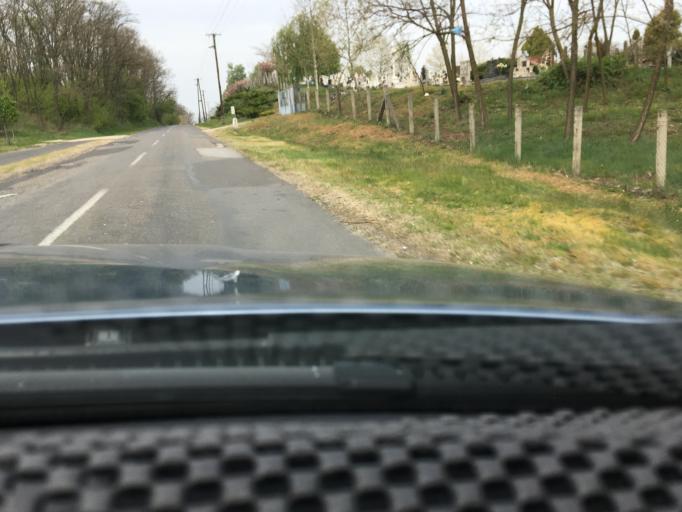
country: HU
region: Szabolcs-Szatmar-Bereg
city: Nyirlugos
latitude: 47.6921
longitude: 22.0300
